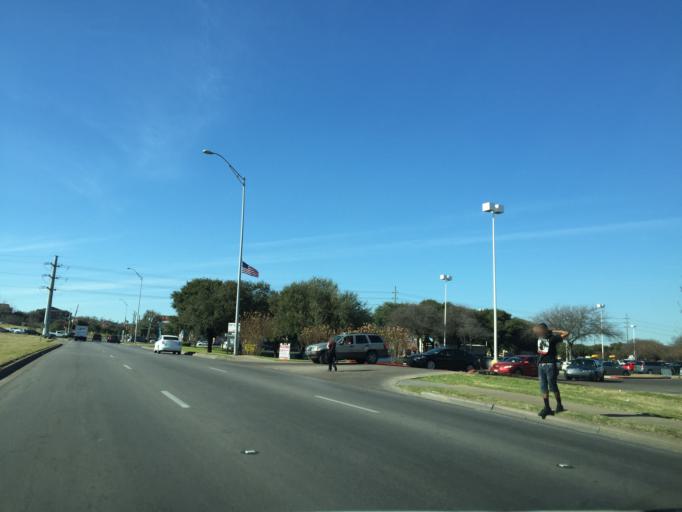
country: US
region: Texas
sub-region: Travis County
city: Austin
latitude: 30.2330
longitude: -97.7213
